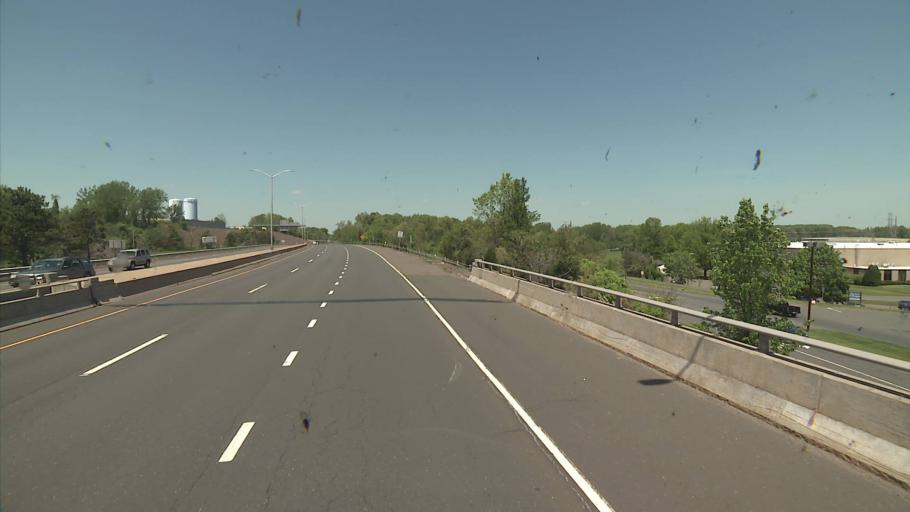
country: US
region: Connecticut
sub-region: Hartford County
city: East Hartford
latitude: 41.7933
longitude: -72.5714
